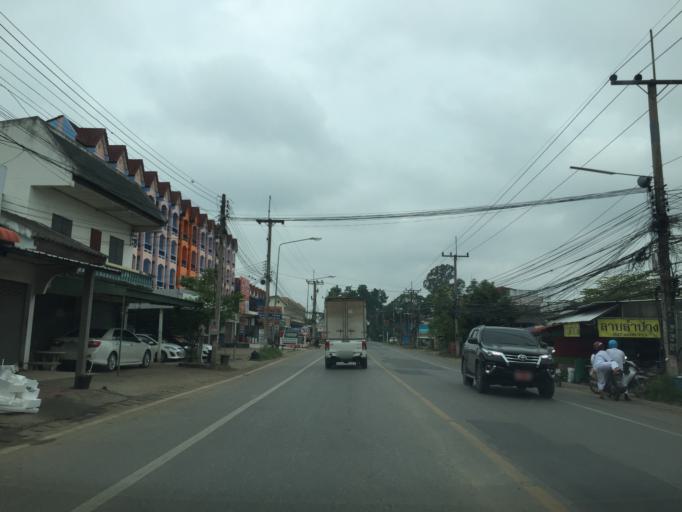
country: TH
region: Lamphun
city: Lamphun
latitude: 18.5823
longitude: 99.0646
